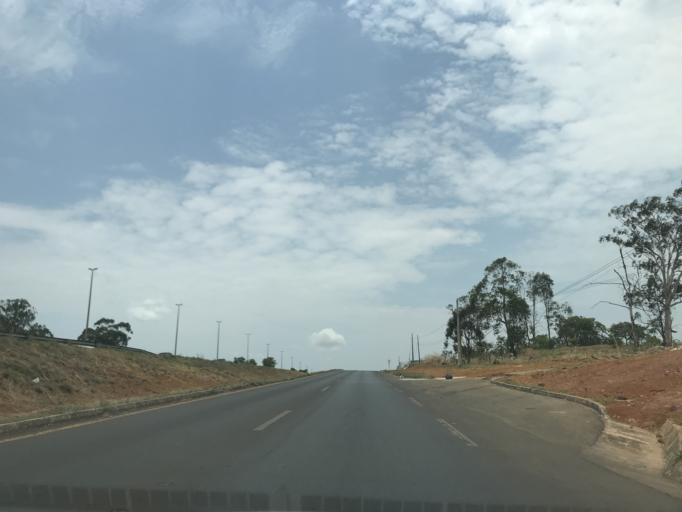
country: BR
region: Federal District
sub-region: Brasilia
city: Brasilia
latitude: -15.6716
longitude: -47.8185
